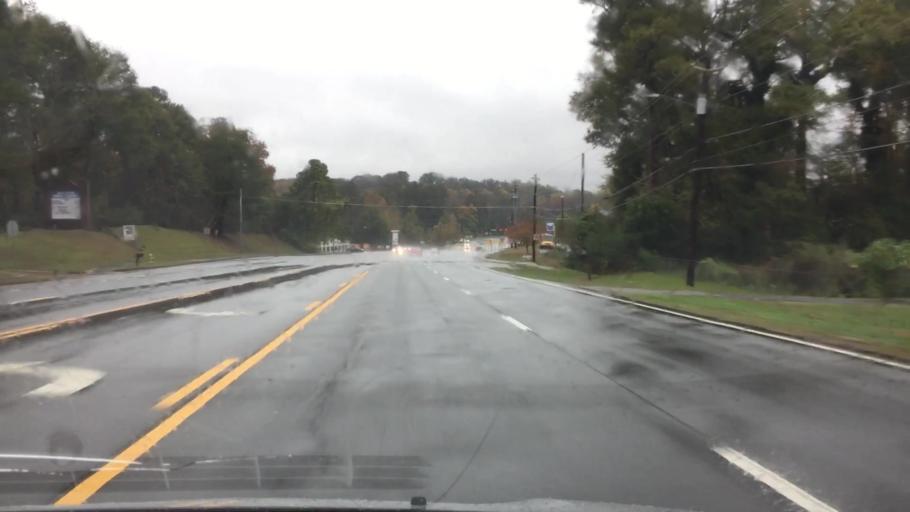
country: US
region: Georgia
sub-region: DeKalb County
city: Panthersville
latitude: 33.6839
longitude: -84.1985
